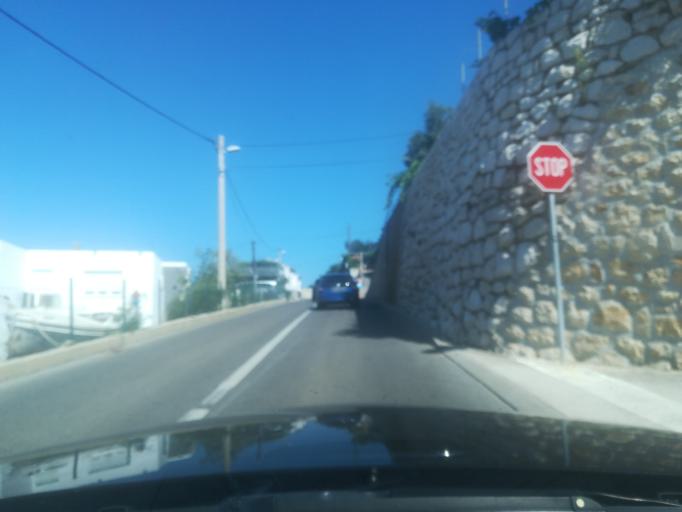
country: HR
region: Primorsko-Goranska
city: Supetarska Draga
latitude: 44.8085
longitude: 14.7197
